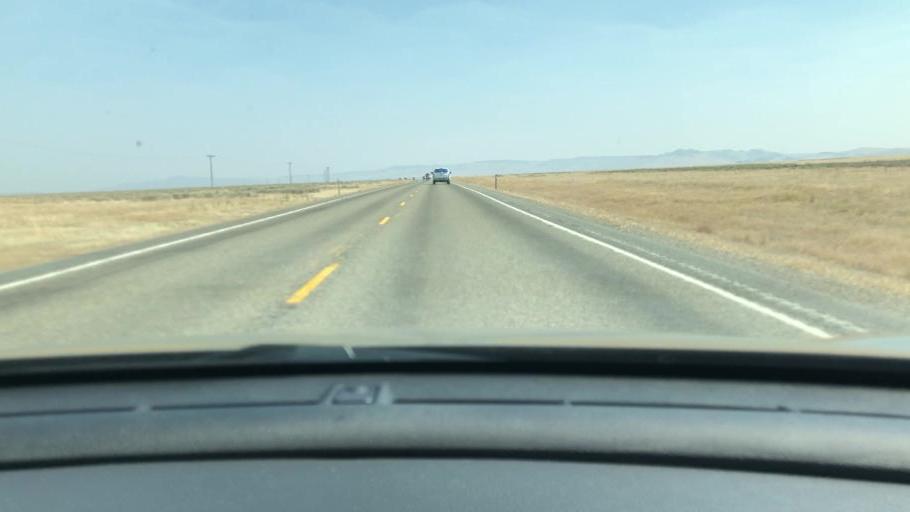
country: US
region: Nevada
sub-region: Humboldt County
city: Winnemucca
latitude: 41.8519
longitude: -117.7117
